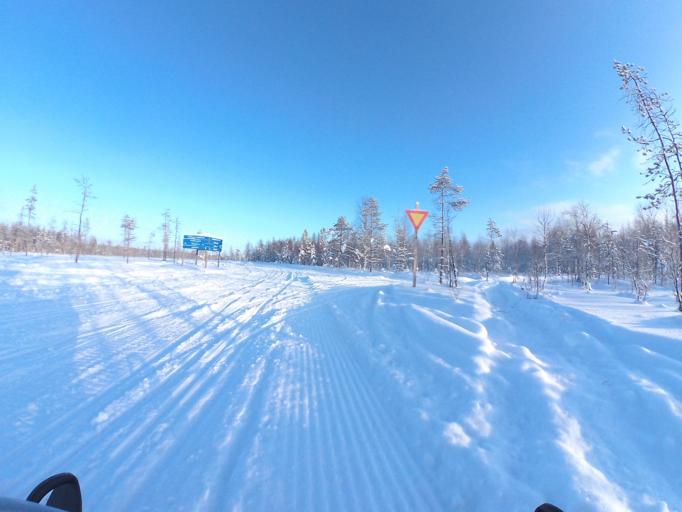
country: FI
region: Lapland
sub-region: Rovaniemi
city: Rovaniemi
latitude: 66.5964
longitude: 25.8613
